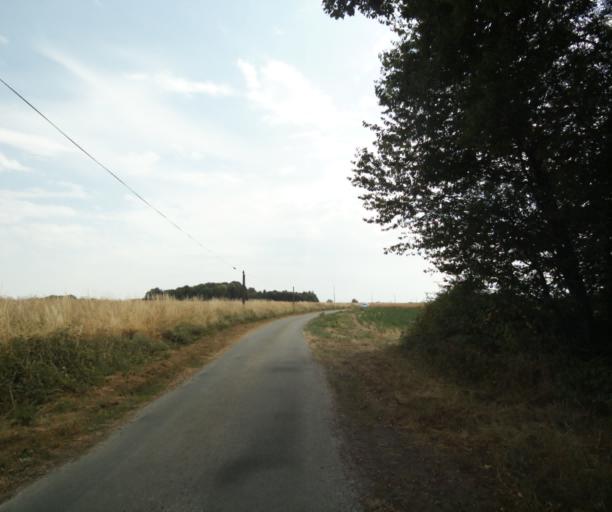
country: FR
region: Centre
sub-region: Departement d'Eure-et-Loir
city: La Bazoche-Gouet
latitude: 48.1851
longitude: 0.9490
